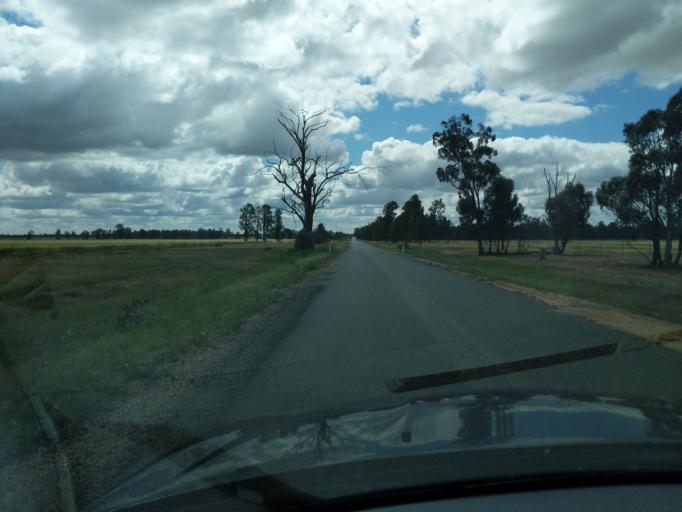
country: AU
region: New South Wales
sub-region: Coolamon
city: Coolamon
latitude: -34.8573
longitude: 146.8986
